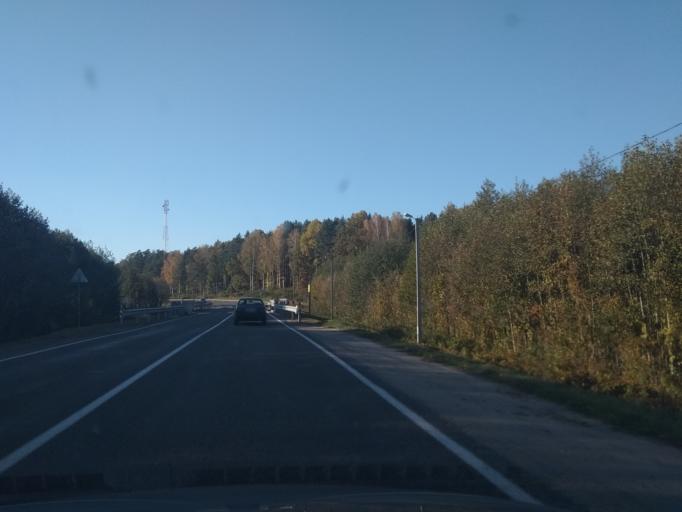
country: BY
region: Grodnenskaya
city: Vyalikaya Byerastavitsa
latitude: 53.1194
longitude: 23.9209
